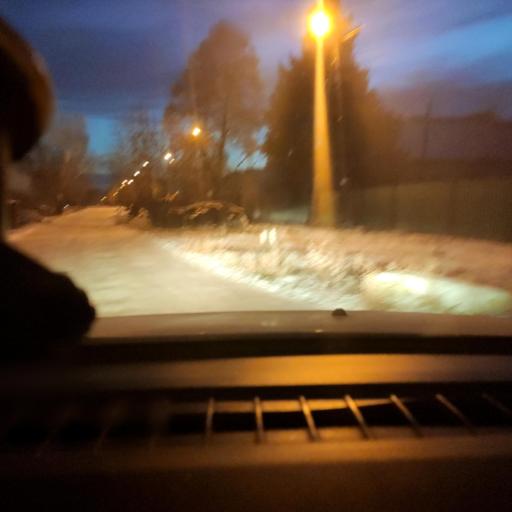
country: RU
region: Samara
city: Petra-Dubrava
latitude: 53.2583
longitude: 50.3344
